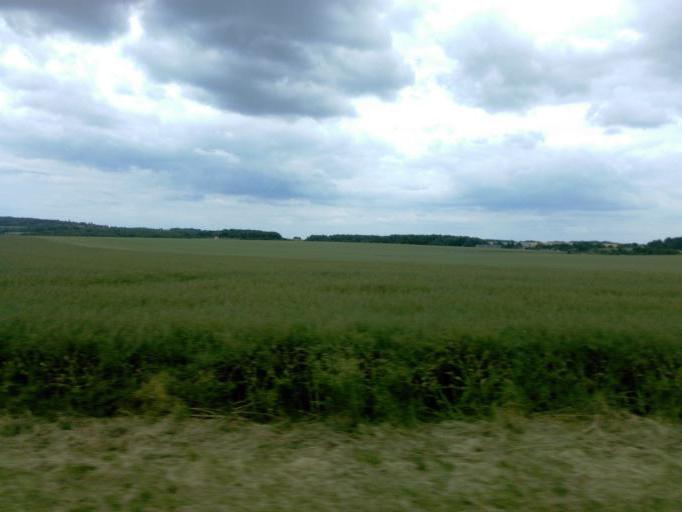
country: FR
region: Ile-de-France
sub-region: Departement du Val-d'Oise
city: Osny
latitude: 49.0991
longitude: 2.0459
